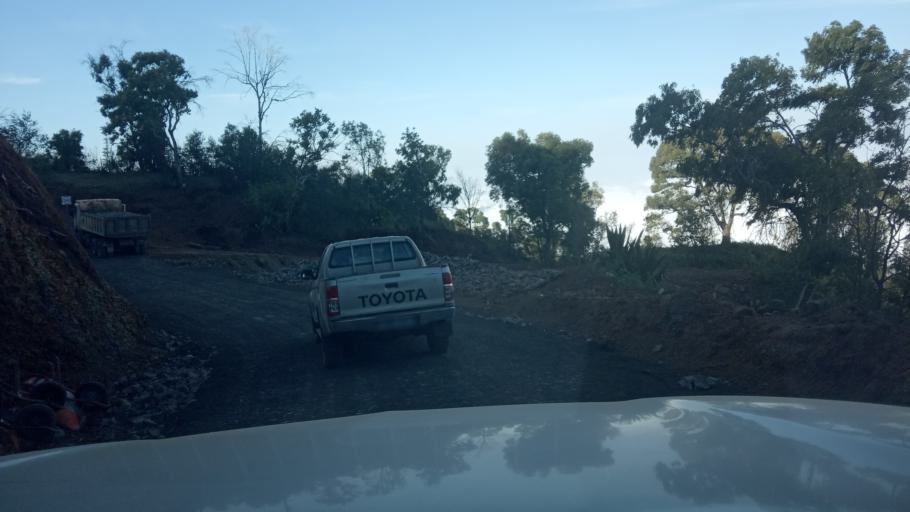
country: CV
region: Mosteiros
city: Porto dos Mosteiros
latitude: 14.9991
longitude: -24.3453
